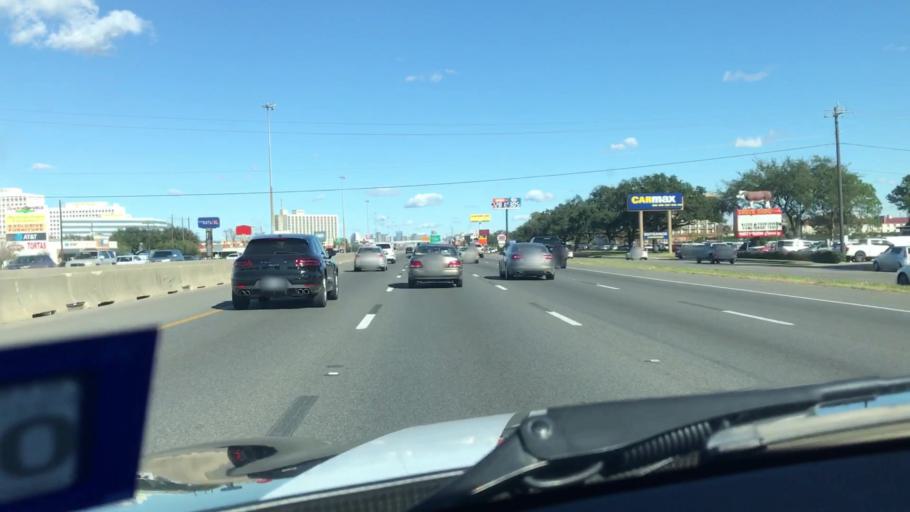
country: US
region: Texas
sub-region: Harris County
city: Bellaire
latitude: 29.7089
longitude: -95.5079
